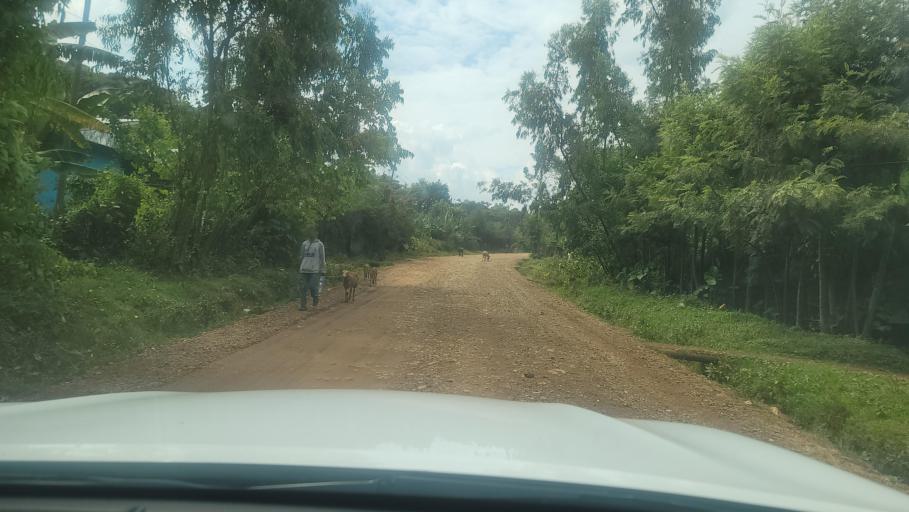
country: ET
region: Oromiya
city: Agaro
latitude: 7.8303
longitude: 36.5431
